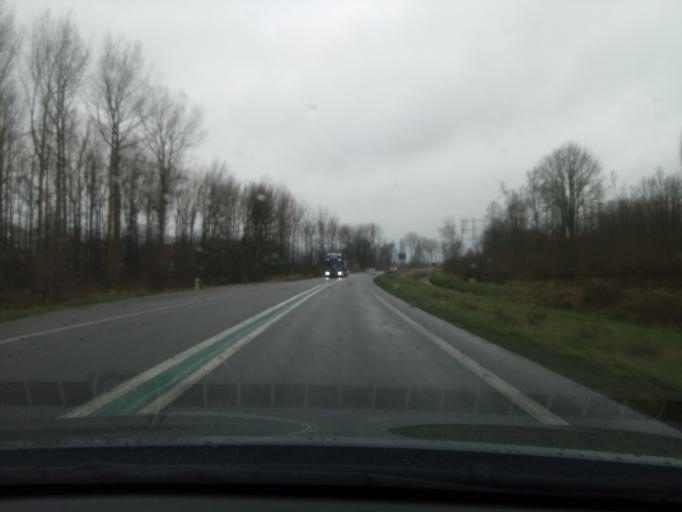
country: NL
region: Groningen
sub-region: Gemeente Appingedam
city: Appingedam
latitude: 53.2727
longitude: 6.8730
